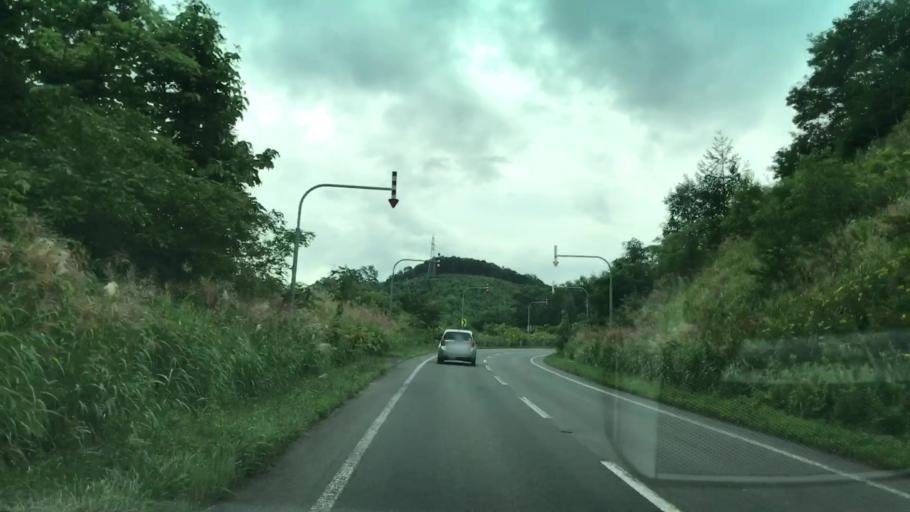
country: JP
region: Hokkaido
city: Yoichi
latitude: 43.1452
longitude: 140.8207
